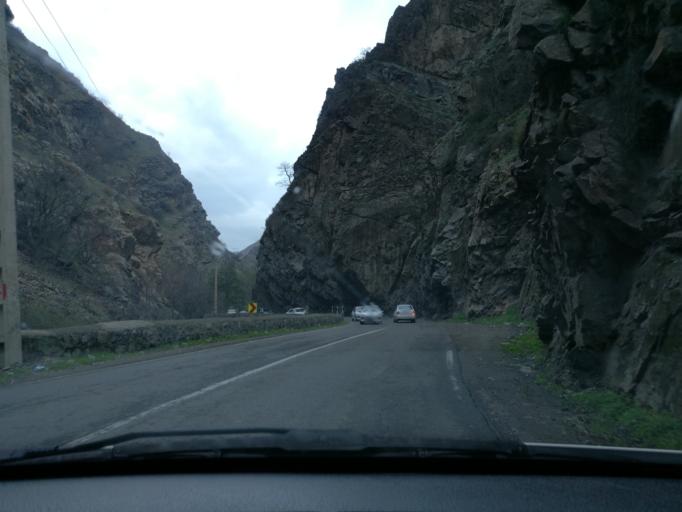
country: IR
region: Mazandaran
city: Chalus
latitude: 36.2959
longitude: 51.2460
